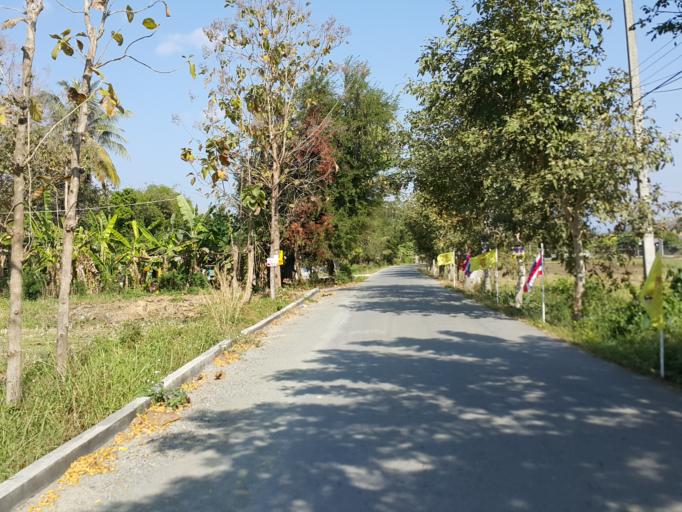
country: TH
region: Chiang Mai
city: San Kamphaeng
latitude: 18.8044
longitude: 99.1486
